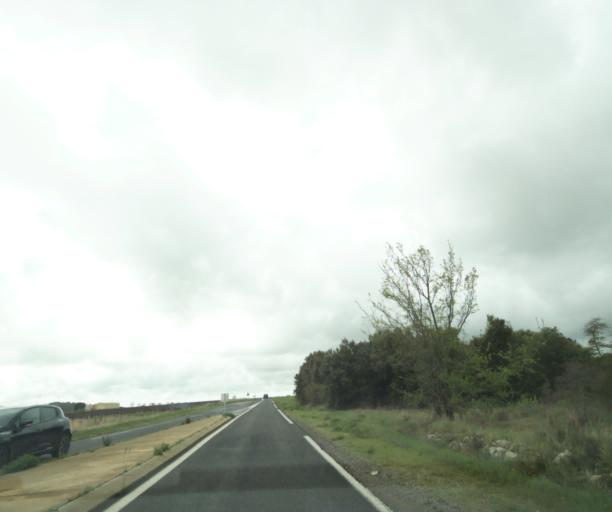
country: FR
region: Languedoc-Roussillon
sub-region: Departement de l'Herault
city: Cournonsec
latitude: 43.5400
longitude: 3.6995
